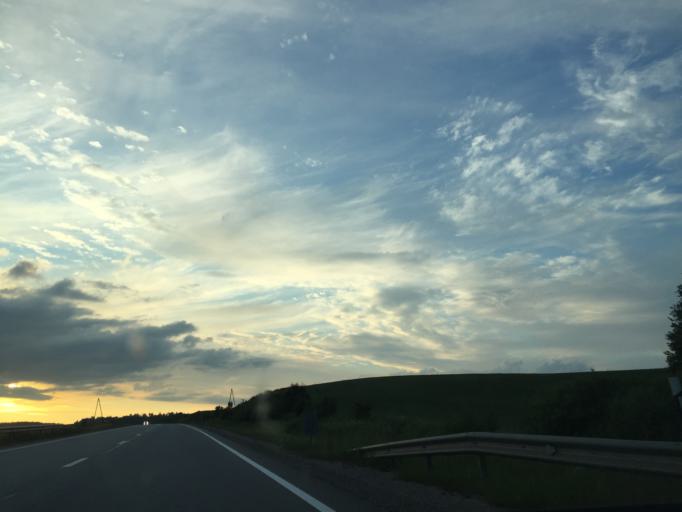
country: LV
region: Tukuma Rajons
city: Tukums
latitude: 56.9727
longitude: 23.0584
